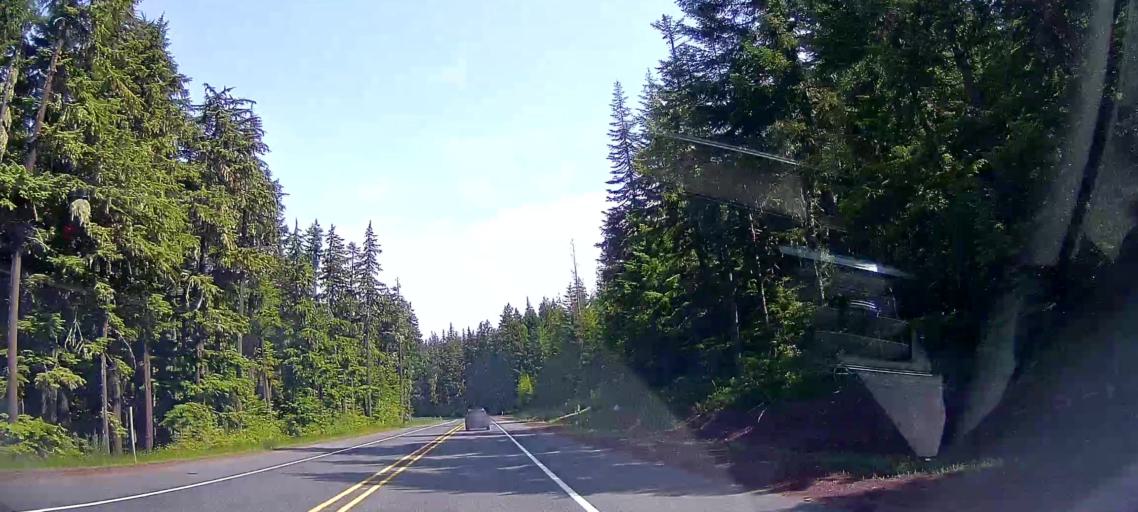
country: US
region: Oregon
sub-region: Clackamas County
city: Mount Hood Village
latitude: 45.1996
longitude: -121.6925
